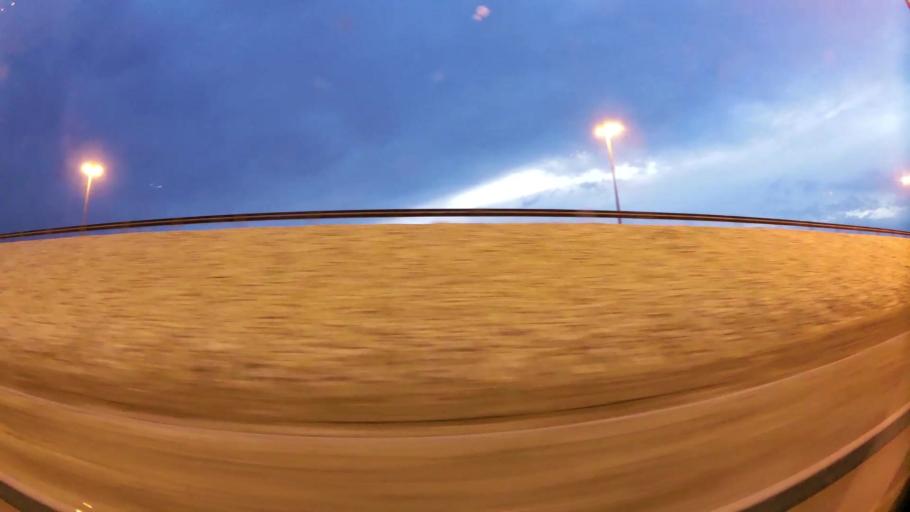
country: BH
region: Central Governorate
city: Madinat Hamad
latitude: 26.1421
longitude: 50.5108
